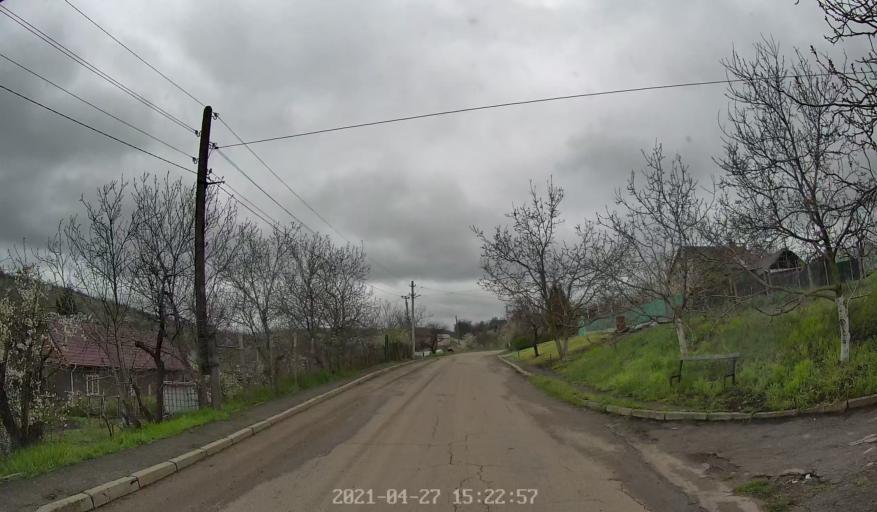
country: MD
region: Chisinau
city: Vadul lui Voda
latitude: 47.0256
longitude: 29.0248
